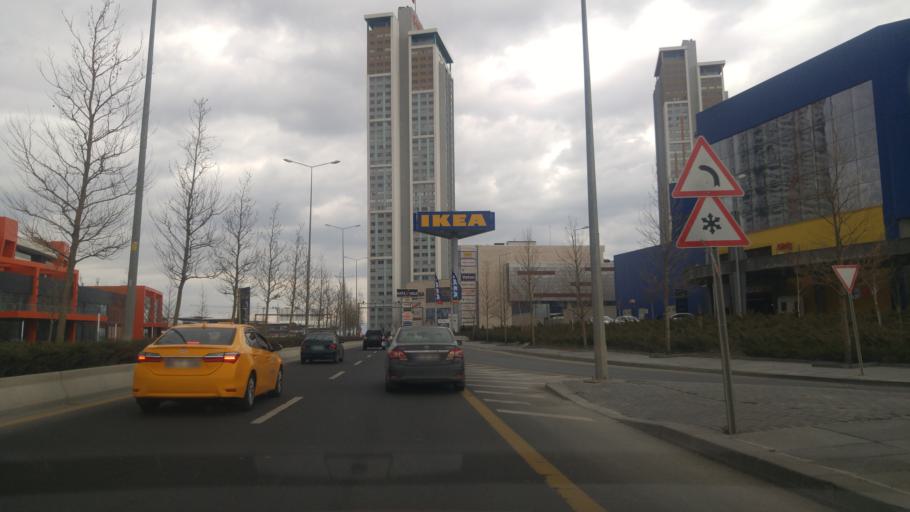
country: TR
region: Ankara
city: Mamak
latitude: 39.8888
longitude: 32.9312
